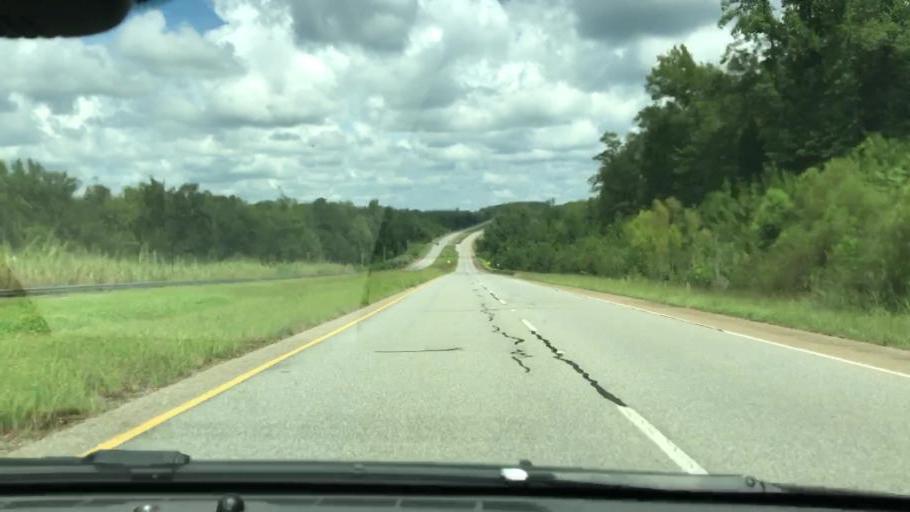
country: US
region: Georgia
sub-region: Stewart County
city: Lumpkin
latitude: 32.0986
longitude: -84.8102
